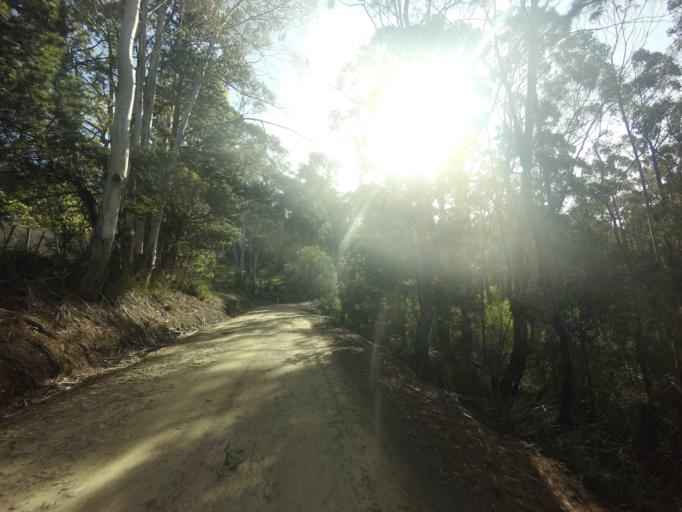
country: AU
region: Tasmania
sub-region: Kingborough
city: Kettering
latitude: -43.1036
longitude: 147.2601
